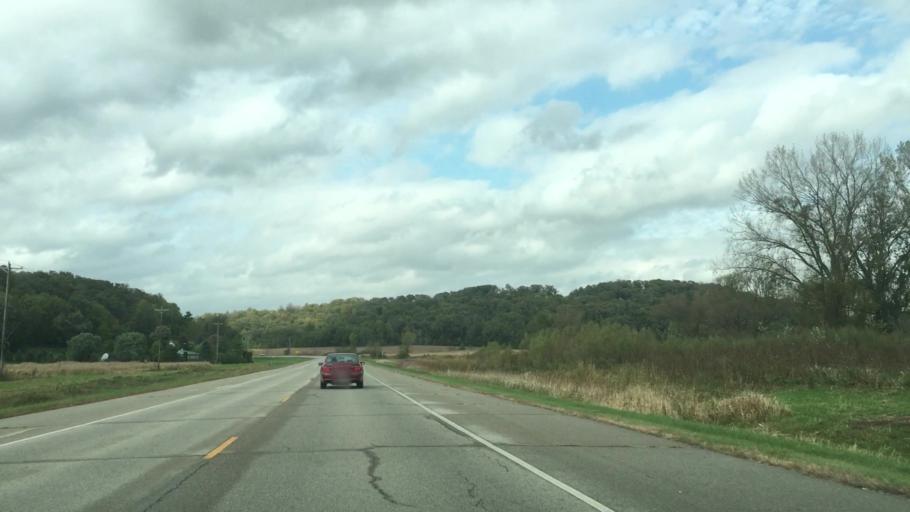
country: US
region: Minnesota
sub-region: Fillmore County
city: Chatfield
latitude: 43.8885
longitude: -92.2267
